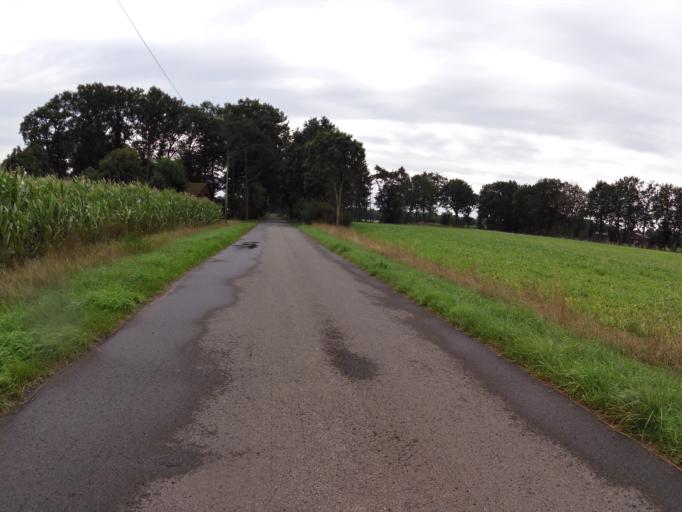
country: DE
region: Lower Saxony
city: Helvesiek
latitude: 53.2115
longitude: 9.4621
